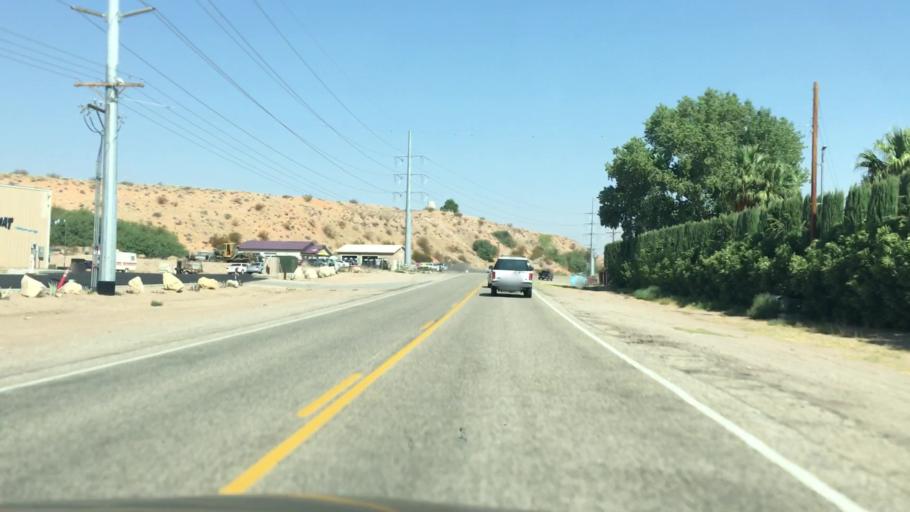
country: US
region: Arizona
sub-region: Mohave County
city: Beaver Dam
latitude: 36.8967
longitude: -113.9332
